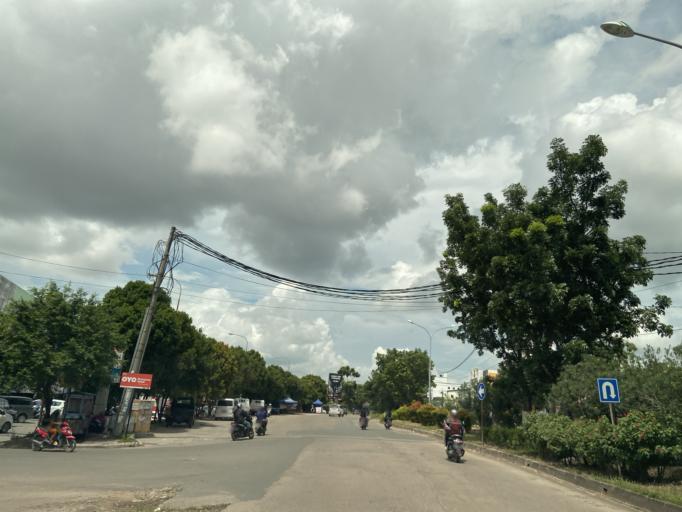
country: SG
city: Singapore
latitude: 1.1387
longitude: 104.0010
